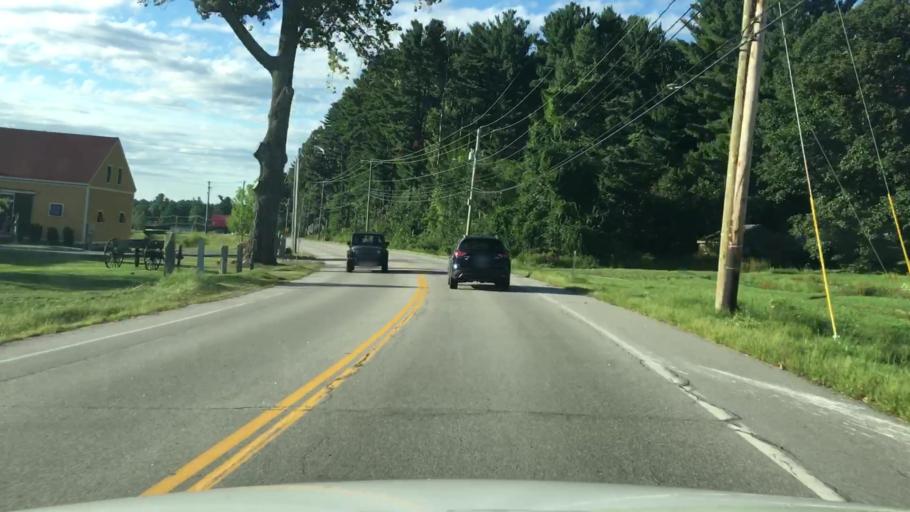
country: US
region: Maine
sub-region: York County
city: Eliot
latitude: 43.1615
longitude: -70.8427
